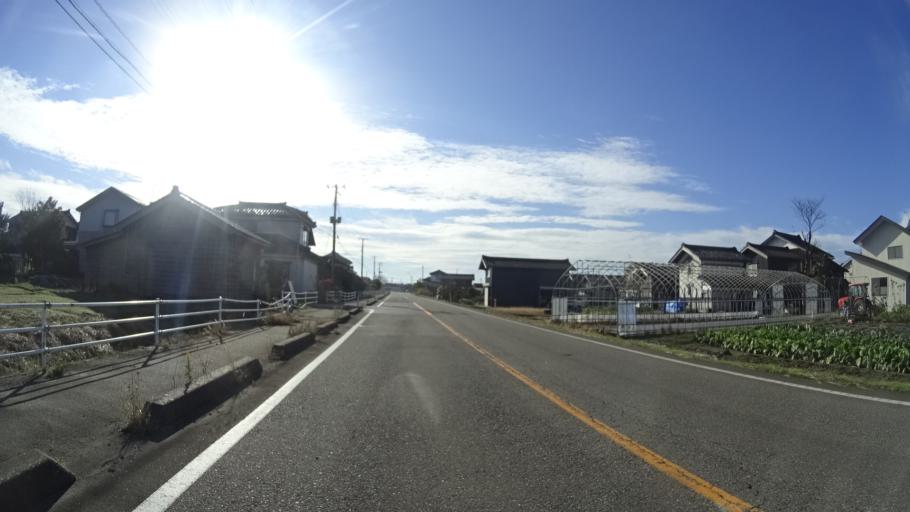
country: JP
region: Niigata
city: Mitsuke
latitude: 37.5797
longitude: 138.8348
